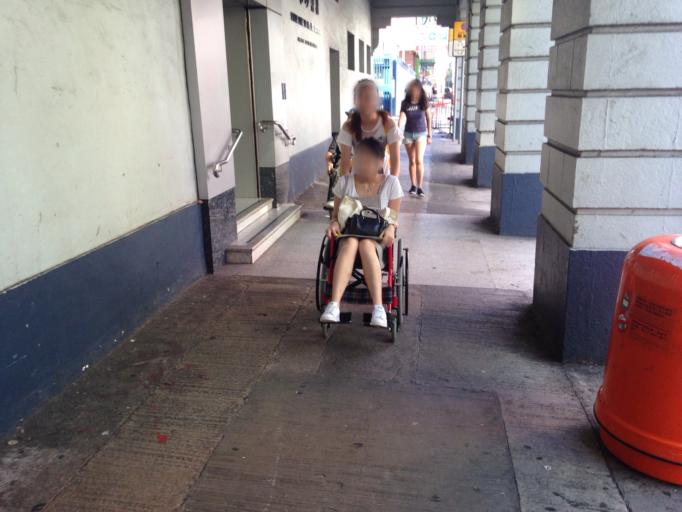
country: HK
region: Sham Shui Po
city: Sham Shui Po
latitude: 22.3300
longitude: 114.1594
